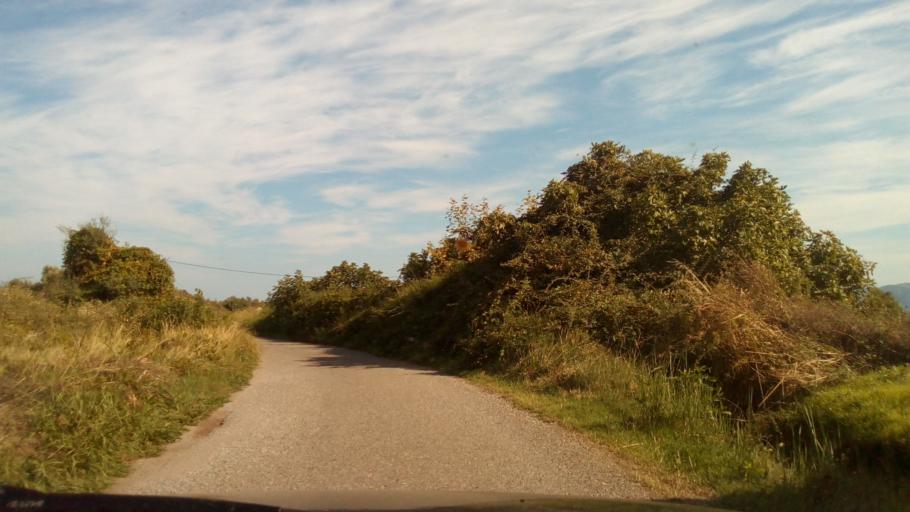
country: GR
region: West Greece
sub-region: Nomos Aitolias kai Akarnanias
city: Nafpaktos
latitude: 38.3957
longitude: 21.9055
